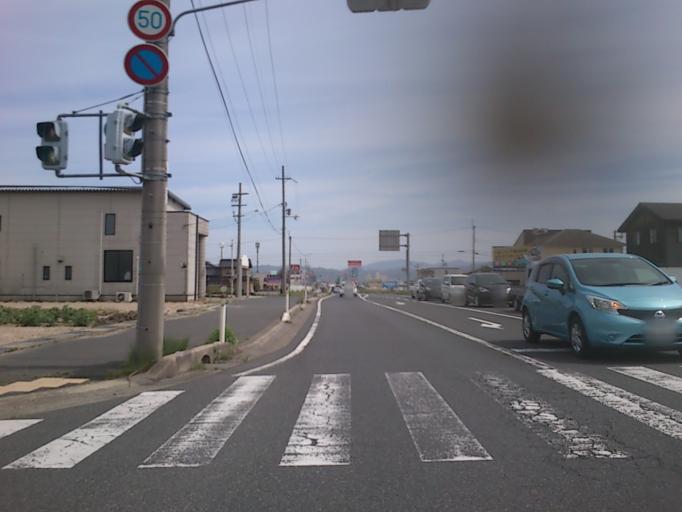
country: JP
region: Kyoto
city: Miyazu
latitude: 35.6196
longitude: 135.0750
